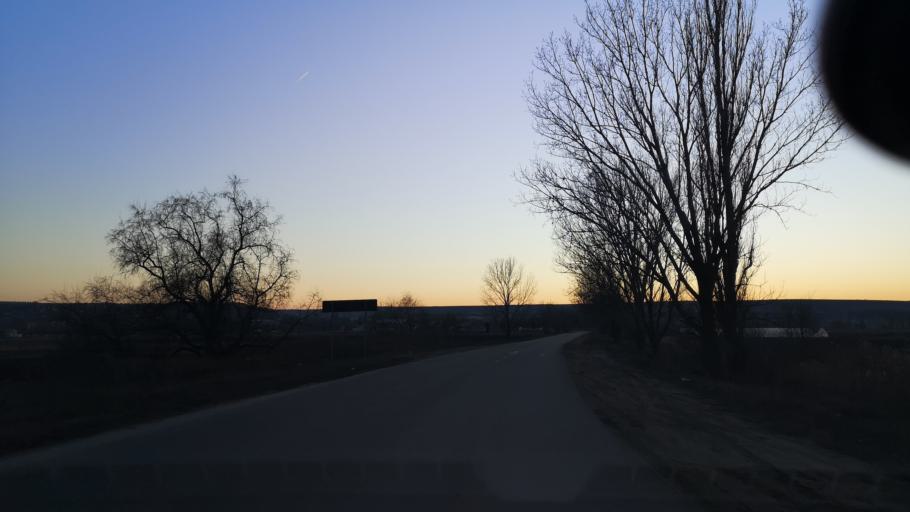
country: MD
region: Anenii Noi
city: Anenii Noi
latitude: 46.8901
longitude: 29.2409
